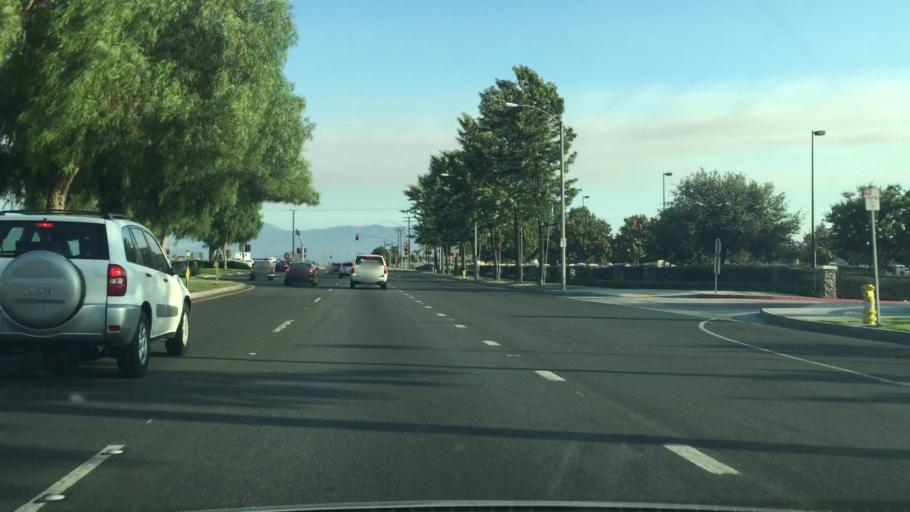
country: US
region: California
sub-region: San Bernardino County
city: Chino
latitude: 34.0209
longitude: -117.6510
